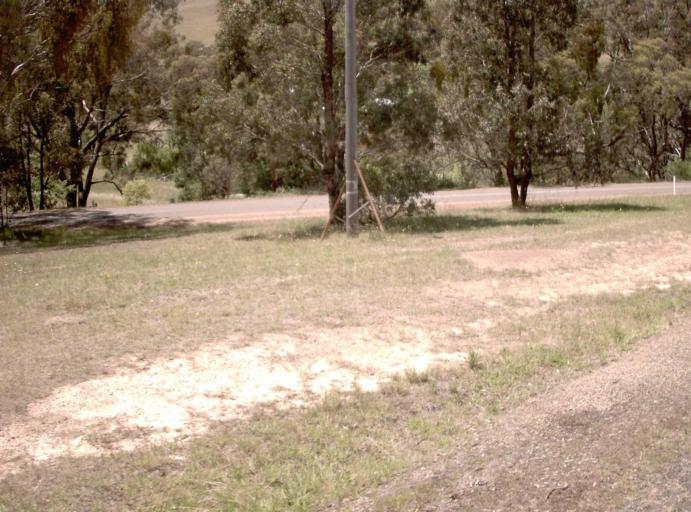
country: AU
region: Victoria
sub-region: East Gippsland
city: Bairnsdale
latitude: -37.3690
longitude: 147.8352
